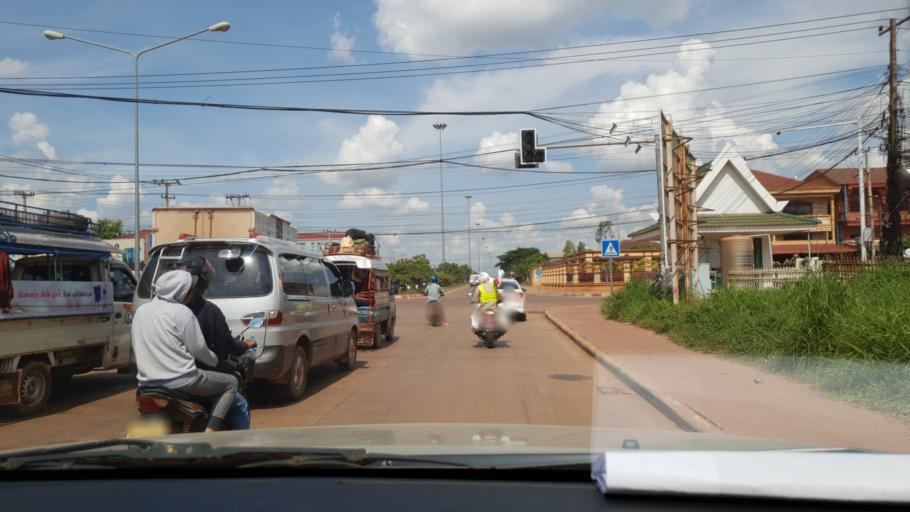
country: LA
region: Vientiane
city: Vientiane
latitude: 18.0309
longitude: 102.6513
